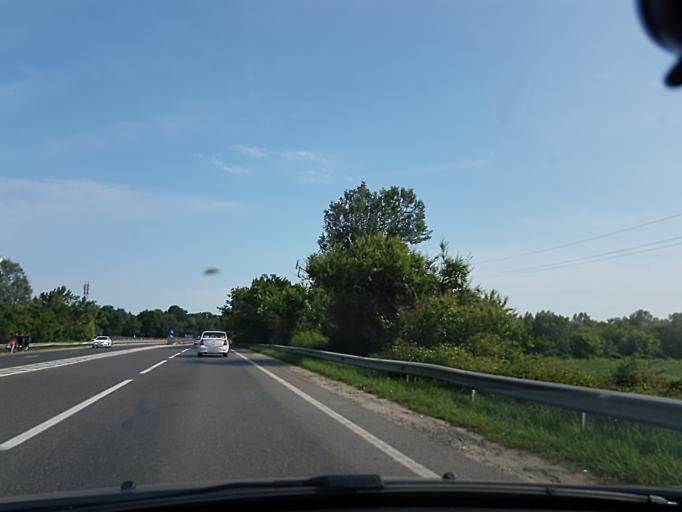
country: RO
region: Ilfov
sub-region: Comuna Ciolpani
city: Ciolpani
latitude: 44.7418
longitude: 26.1117
